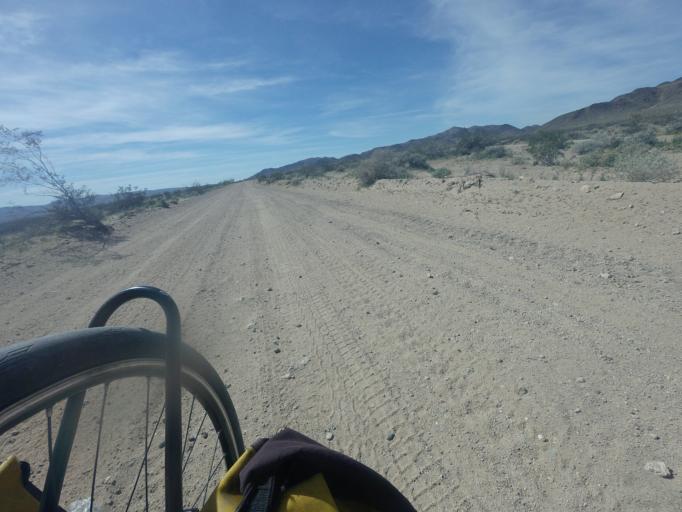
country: US
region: California
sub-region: San Bernardino County
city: Searles Valley
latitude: 35.5733
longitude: -117.4380
